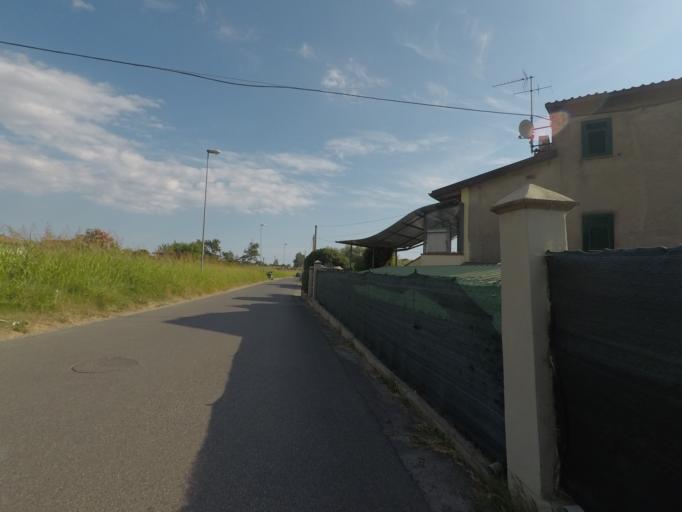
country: IT
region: Tuscany
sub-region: Provincia di Massa-Carrara
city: Capanne-Prato-Cinquale
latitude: 44.0114
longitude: 10.1490
